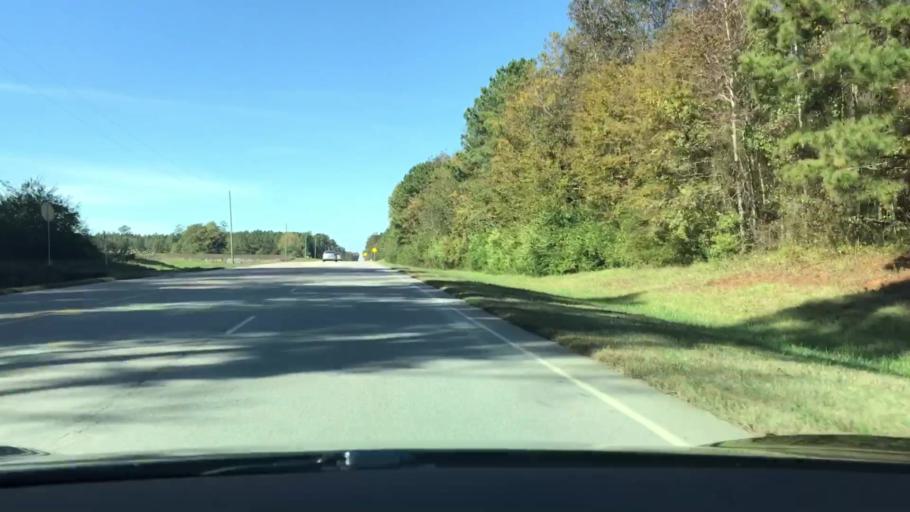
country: US
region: Georgia
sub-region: Warren County
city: Firing Range
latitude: 33.4797
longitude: -82.7481
